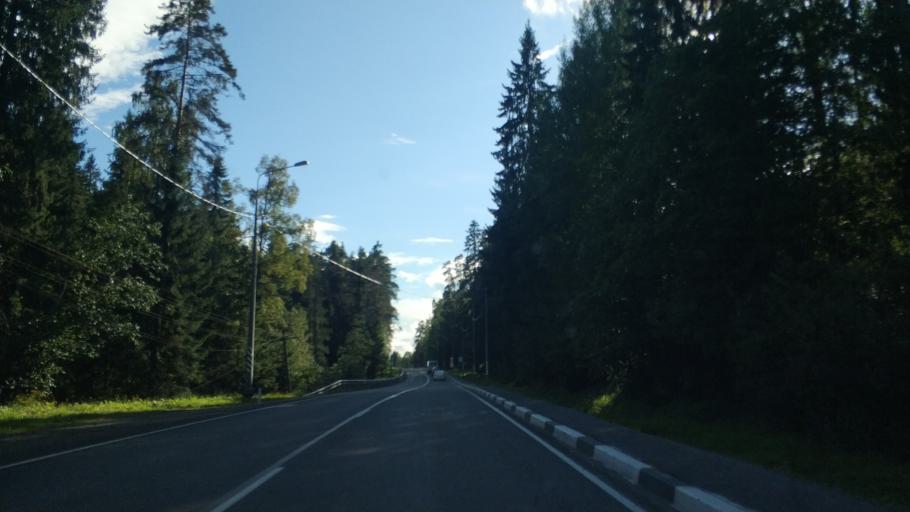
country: RU
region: Republic of Karelia
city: Lakhdenpokh'ya
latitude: 61.5336
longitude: 30.2110
